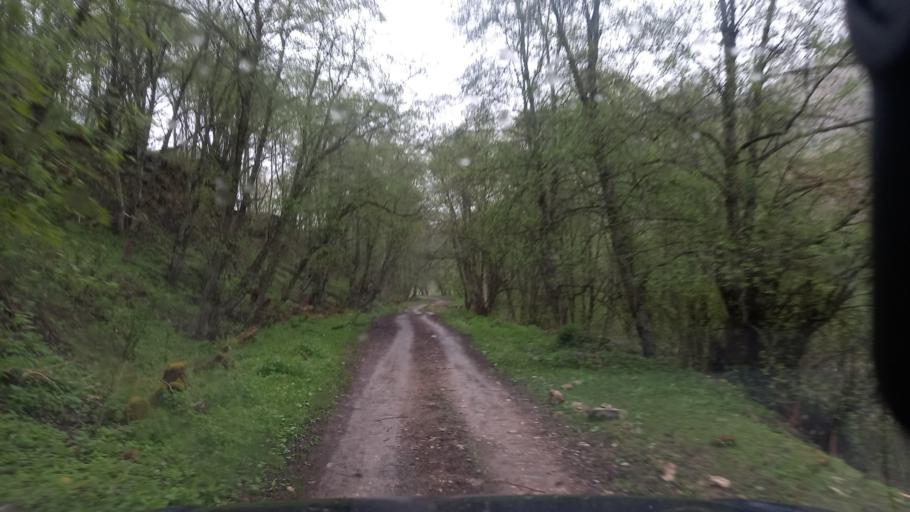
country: RU
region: Kabardino-Balkariya
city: Bylym
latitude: 43.5996
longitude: 42.9217
